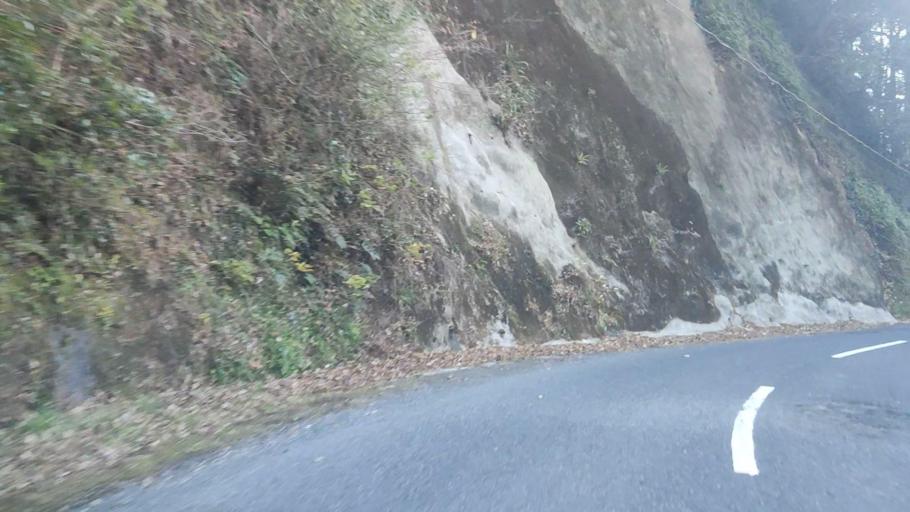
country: JP
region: Kagoshima
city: Kokubu-matsuki
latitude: 31.6694
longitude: 130.8230
